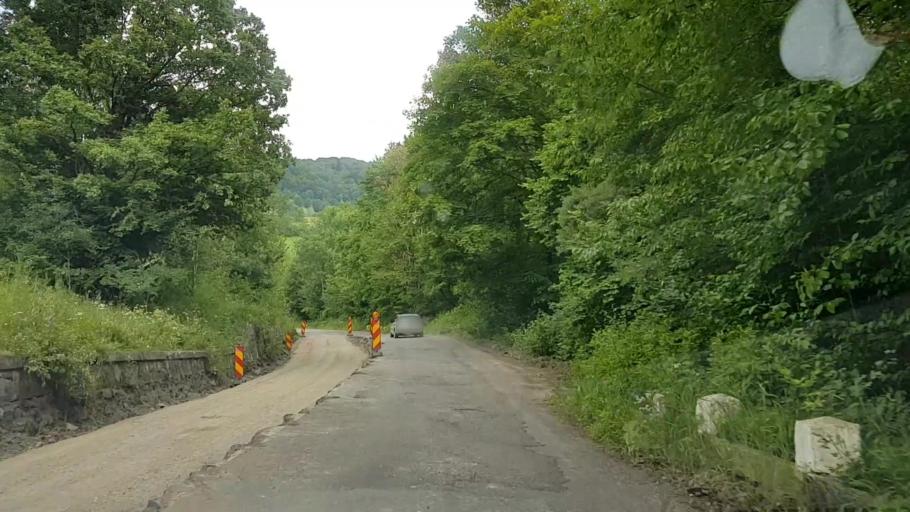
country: RO
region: Neamt
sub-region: Comuna Pangarati
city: Pangarati
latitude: 46.9413
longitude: 26.1248
